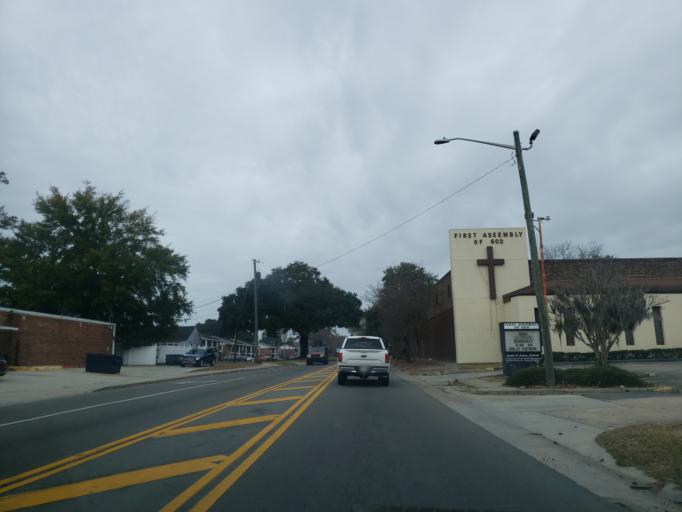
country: US
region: Georgia
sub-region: Chatham County
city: Thunderbolt
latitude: 32.0493
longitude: -81.0650
